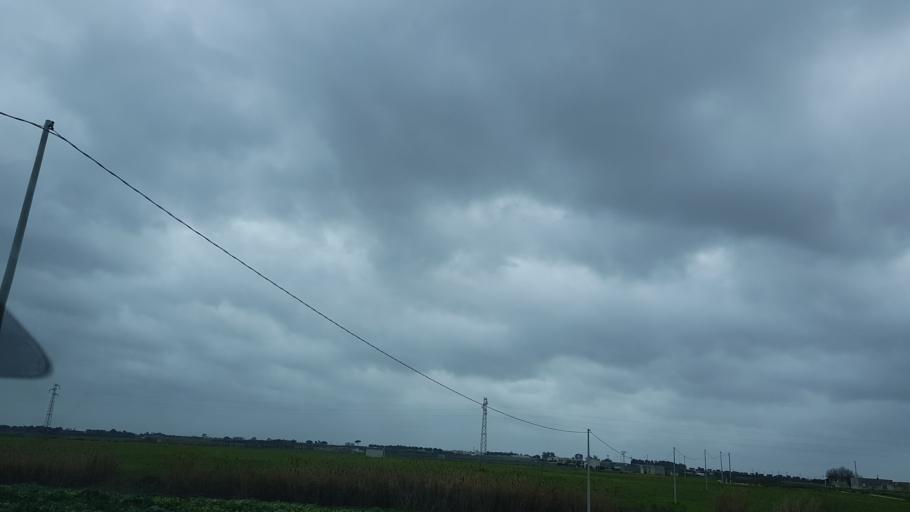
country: IT
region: Apulia
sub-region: Provincia di Brindisi
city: Brindisi
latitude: 40.6631
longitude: 17.8645
